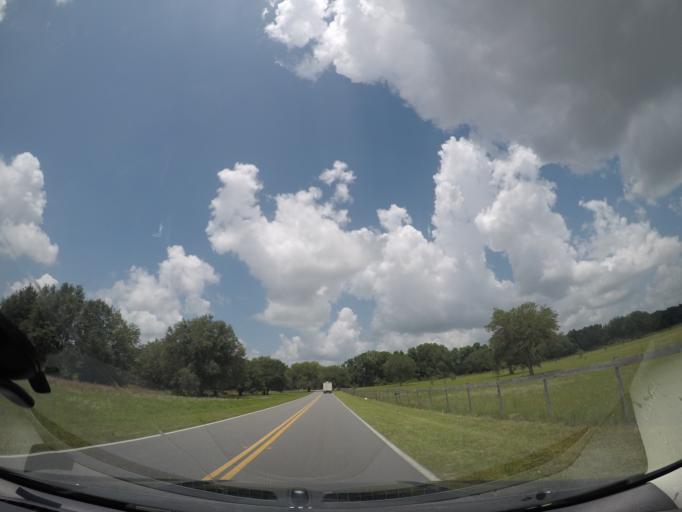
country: US
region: Florida
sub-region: Alachua County
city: High Springs
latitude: 29.8309
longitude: -82.7061
